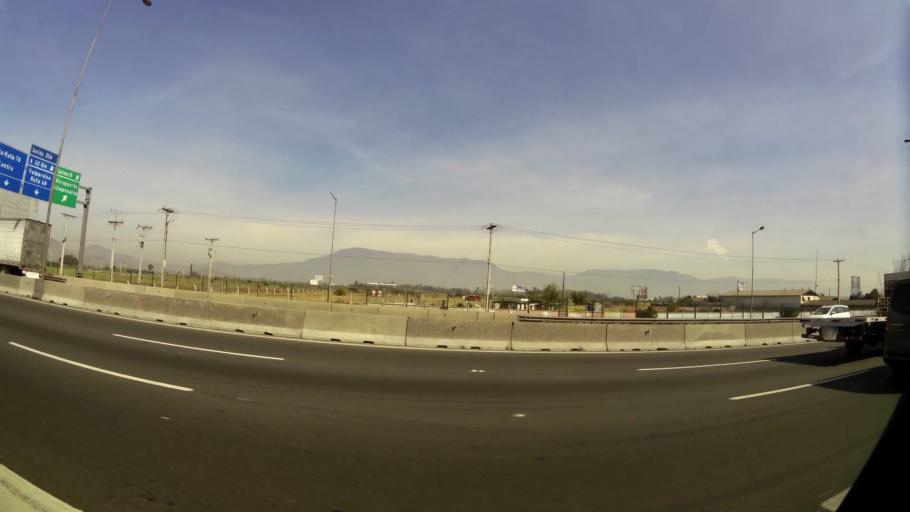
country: CL
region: Santiago Metropolitan
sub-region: Provincia de Santiago
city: Lo Prado
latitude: -33.4199
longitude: -70.7821
